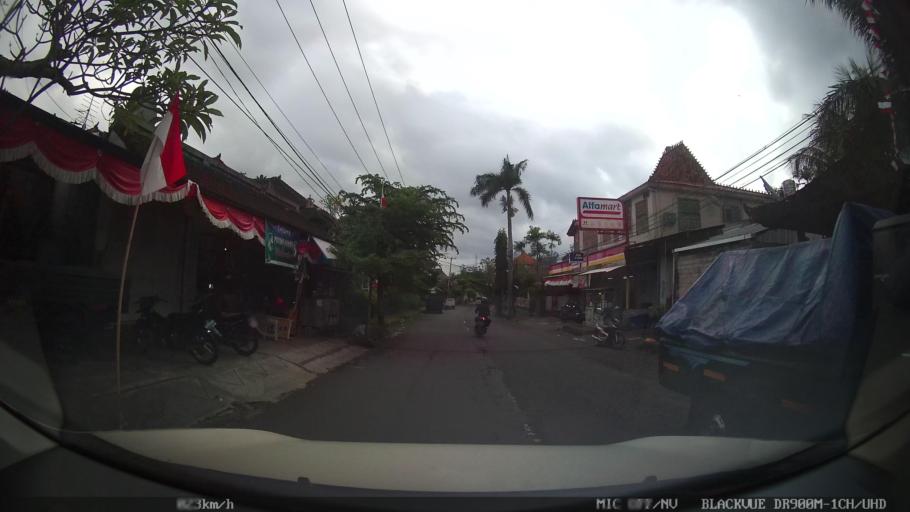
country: ID
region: Bali
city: Banjar Tegal Belodan
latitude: -8.5409
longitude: 115.1207
